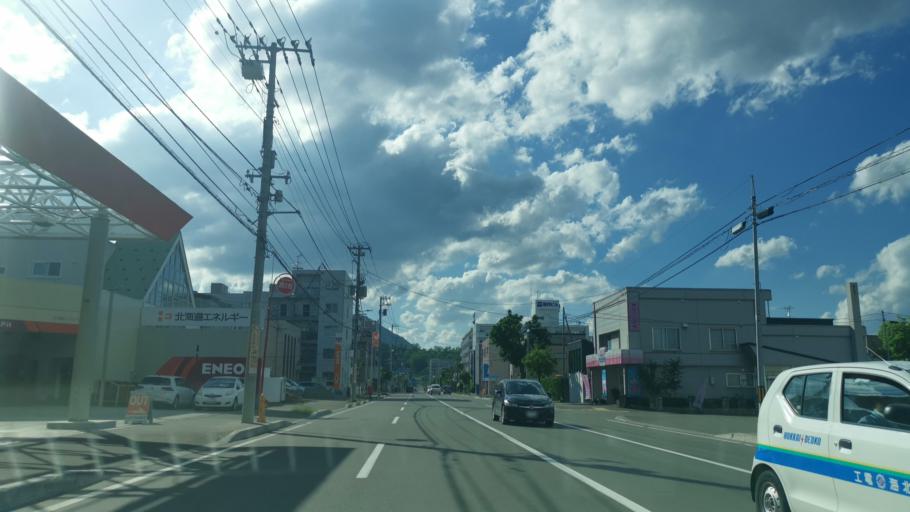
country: JP
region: Hokkaido
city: Sapporo
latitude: 43.0791
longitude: 141.2756
